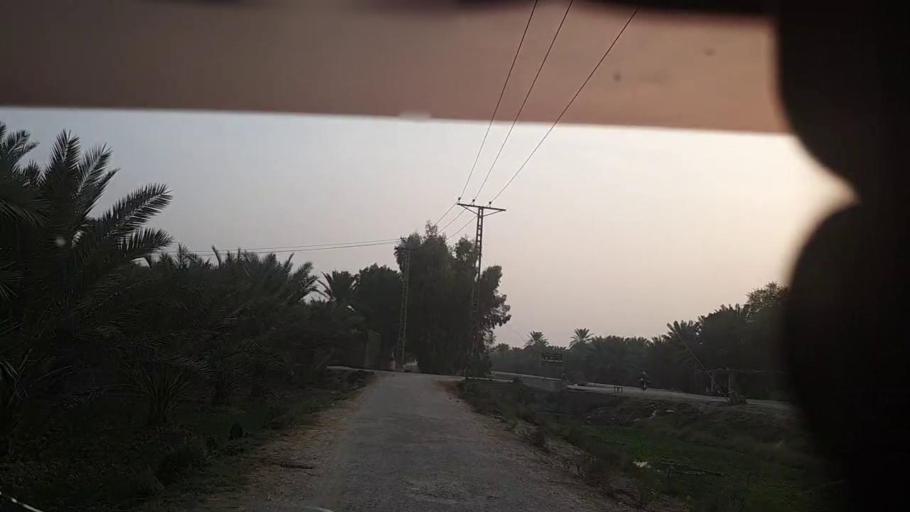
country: PK
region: Sindh
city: Pir jo Goth
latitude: 27.5204
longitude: 68.6391
